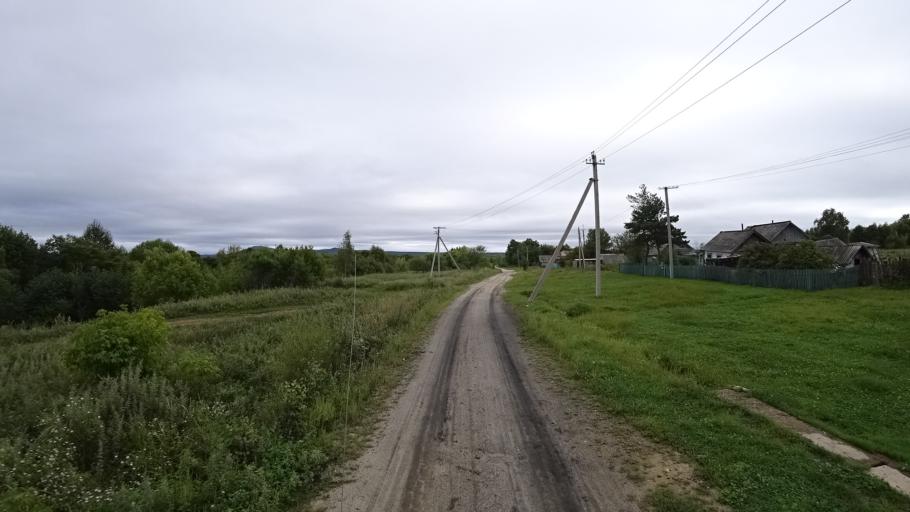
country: RU
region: Primorskiy
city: Rettikhovka
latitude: 44.1390
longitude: 132.6424
